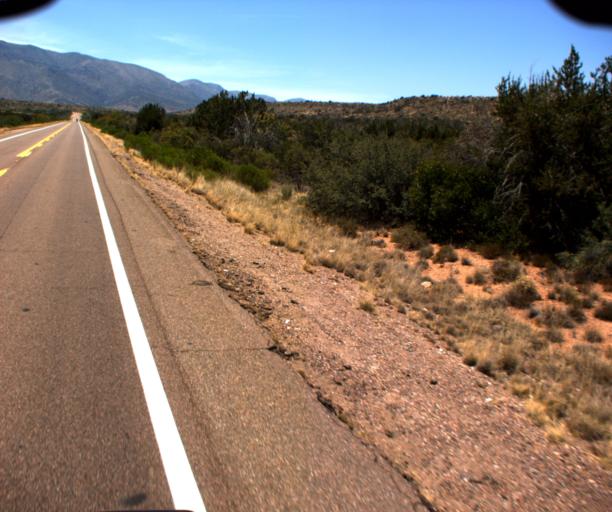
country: US
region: Arizona
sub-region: Gila County
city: Payson
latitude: 34.0295
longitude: -111.3513
